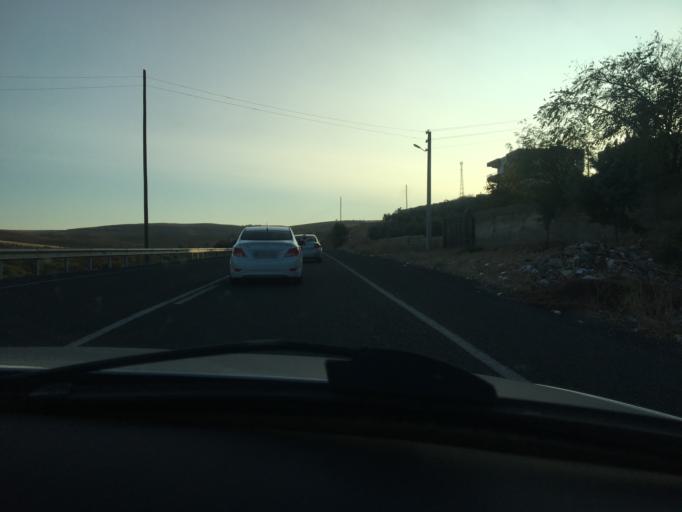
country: TR
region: Sanliurfa
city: Halfeti
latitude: 37.2033
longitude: 37.9702
